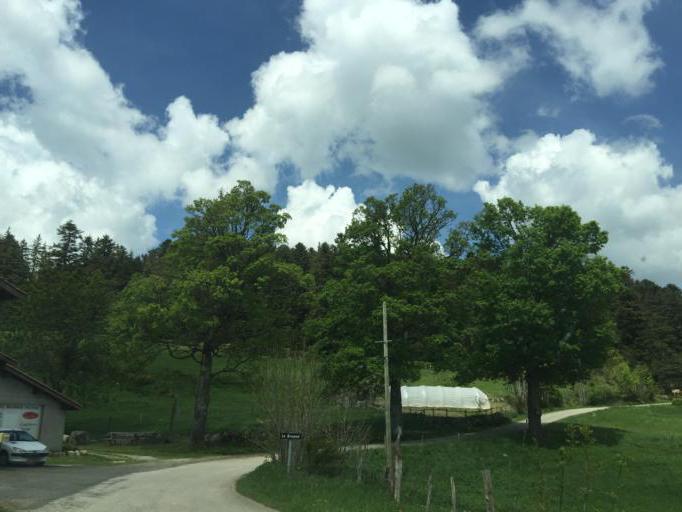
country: FR
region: Rhone-Alpes
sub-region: Departement de la Loire
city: Saint-Sauveur-en-Rue
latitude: 45.2707
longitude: 4.4700
